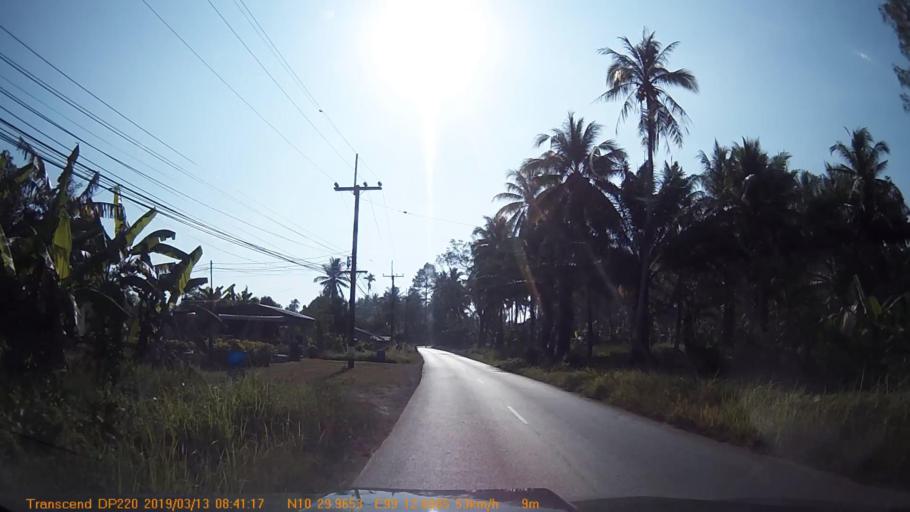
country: TH
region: Chumphon
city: Chumphon
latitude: 10.4994
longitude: 99.2116
